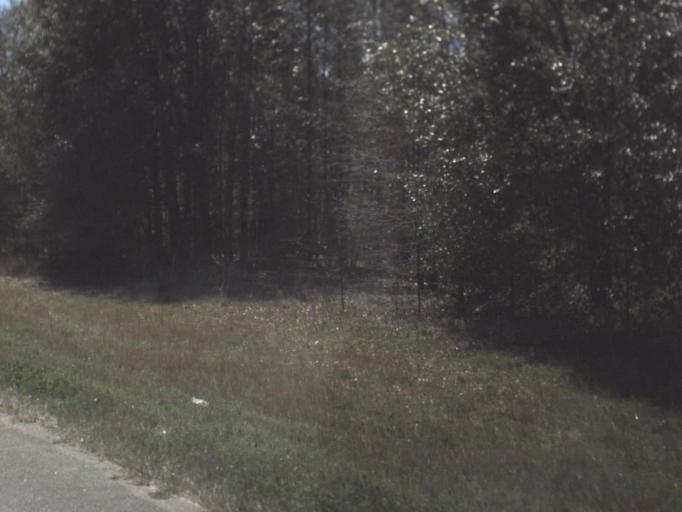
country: US
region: Florida
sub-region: Gadsden County
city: Gretna
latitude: 30.6916
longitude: -84.6225
